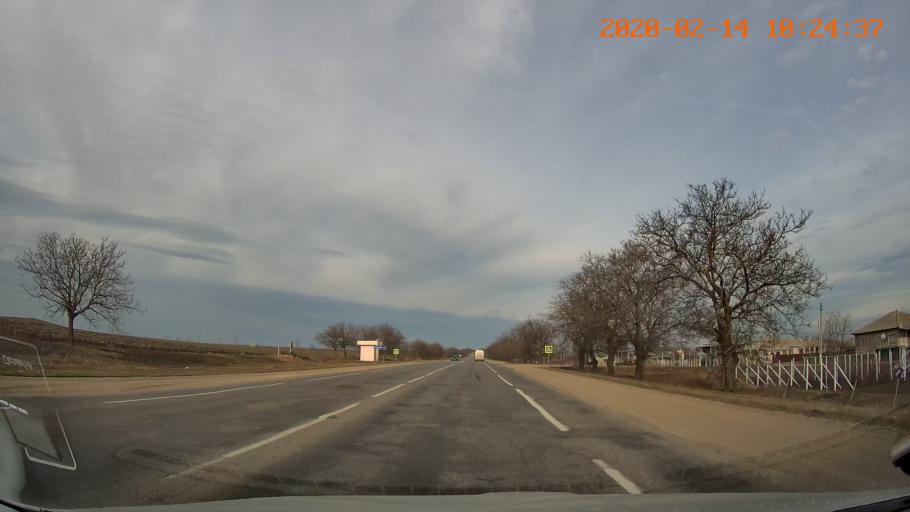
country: MD
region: Balti
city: Balti
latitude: 47.8251
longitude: 27.8200
